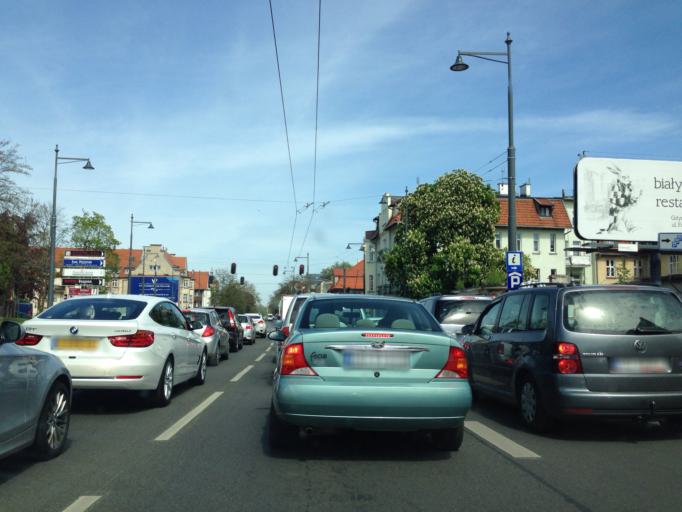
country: PL
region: Pomeranian Voivodeship
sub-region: Sopot
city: Sopot
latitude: 54.4341
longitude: 18.5617
